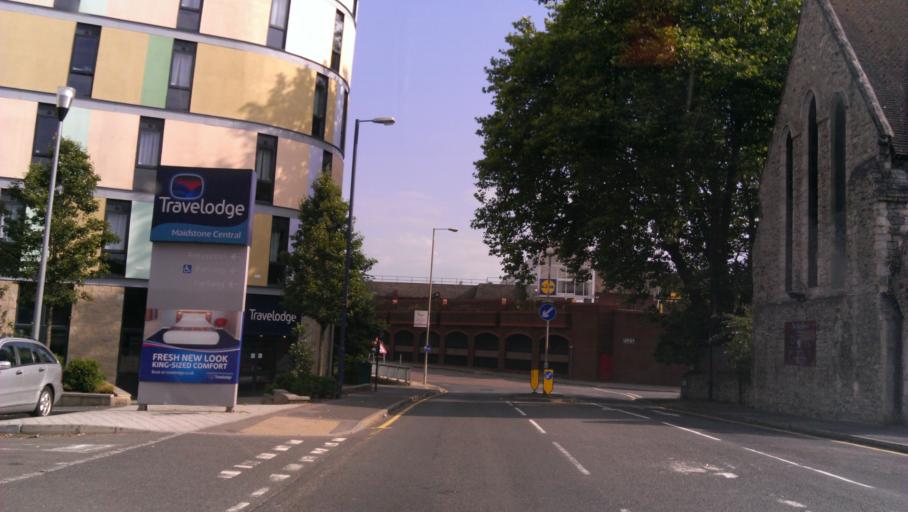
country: GB
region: England
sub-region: Kent
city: Maidstone
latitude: 51.2731
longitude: 0.5163
